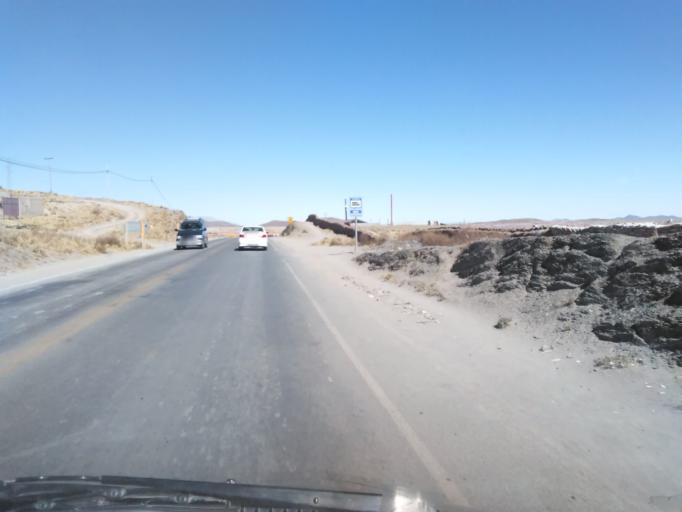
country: BO
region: Oruro
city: Oruro
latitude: -17.9829
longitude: -67.0497
